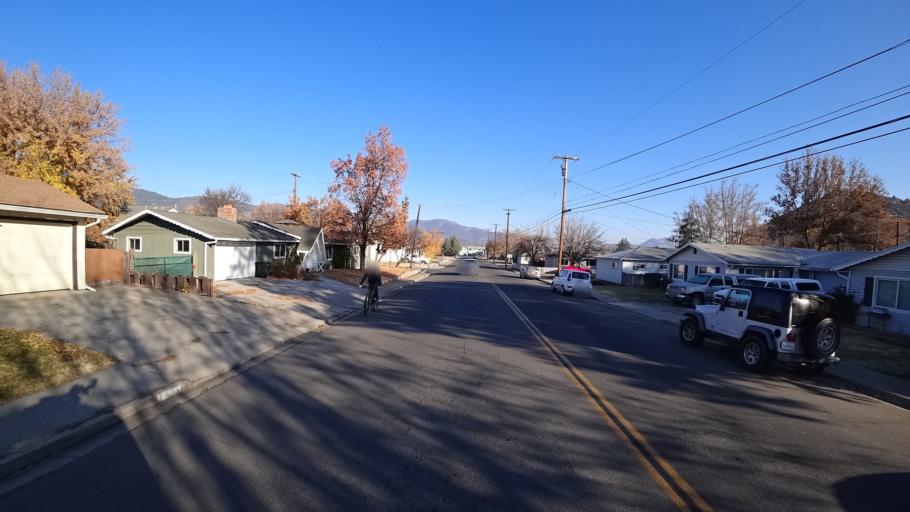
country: US
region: California
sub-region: Siskiyou County
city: Yreka
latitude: 41.7187
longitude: -122.6418
